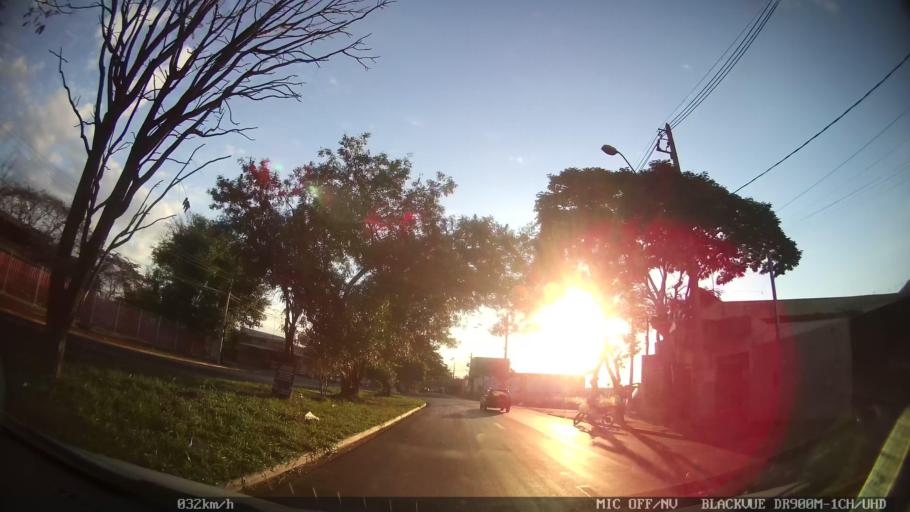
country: BR
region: Sao Paulo
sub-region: Ribeirao Preto
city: Ribeirao Preto
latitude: -21.1382
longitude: -47.7952
